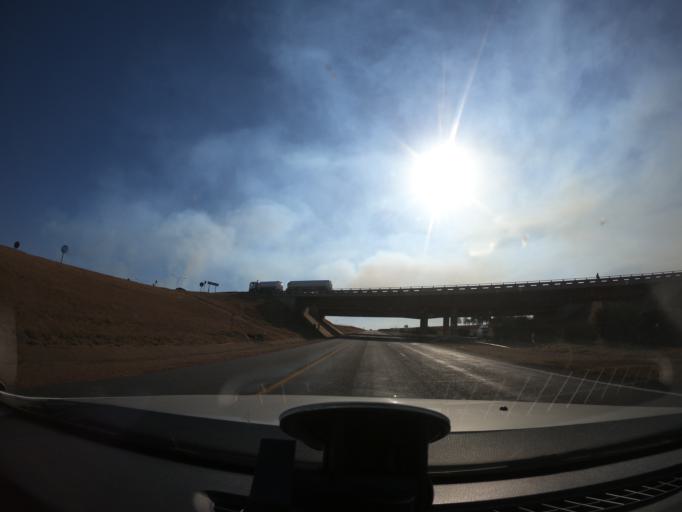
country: ZA
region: Gauteng
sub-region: Sedibeng District Municipality
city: Heidelberg
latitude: -26.4916
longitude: 28.3737
